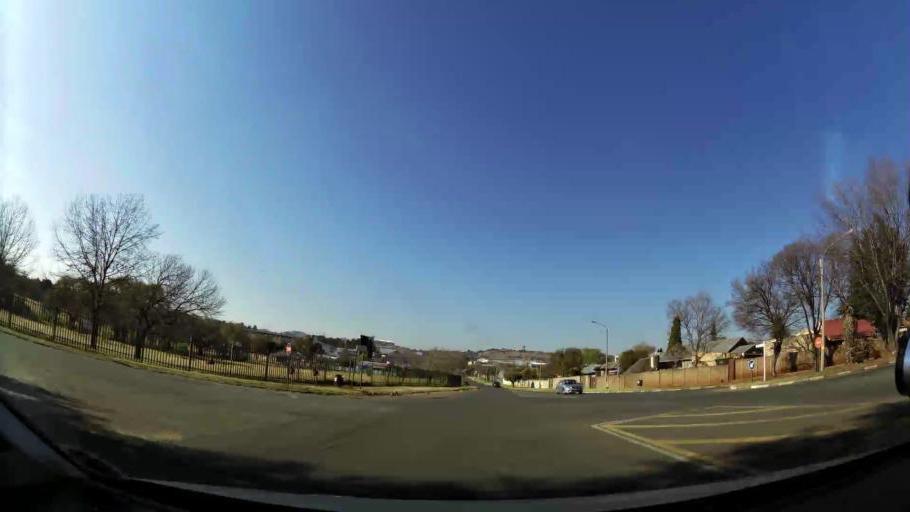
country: ZA
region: Gauteng
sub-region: City of Johannesburg Metropolitan Municipality
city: Modderfontein
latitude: -26.1513
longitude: 28.1657
